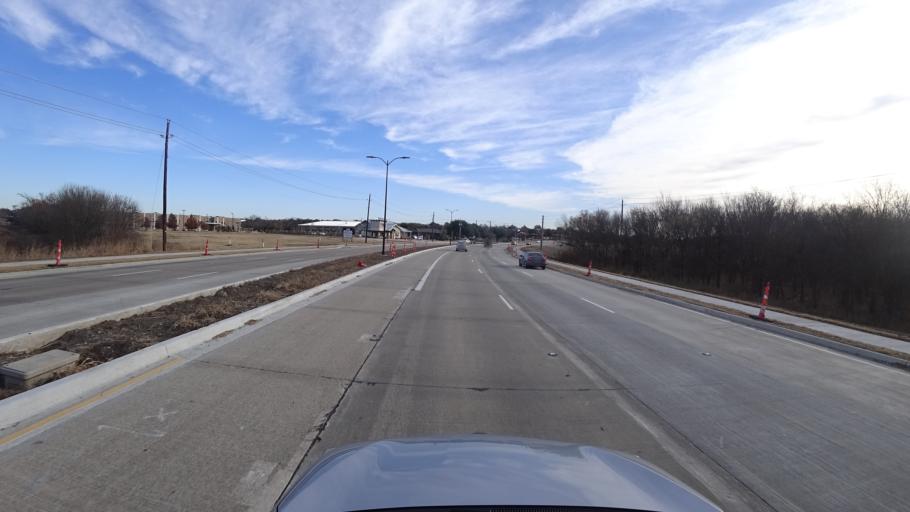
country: US
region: Texas
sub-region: Collin County
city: McKinney
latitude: 33.1983
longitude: -96.6577
